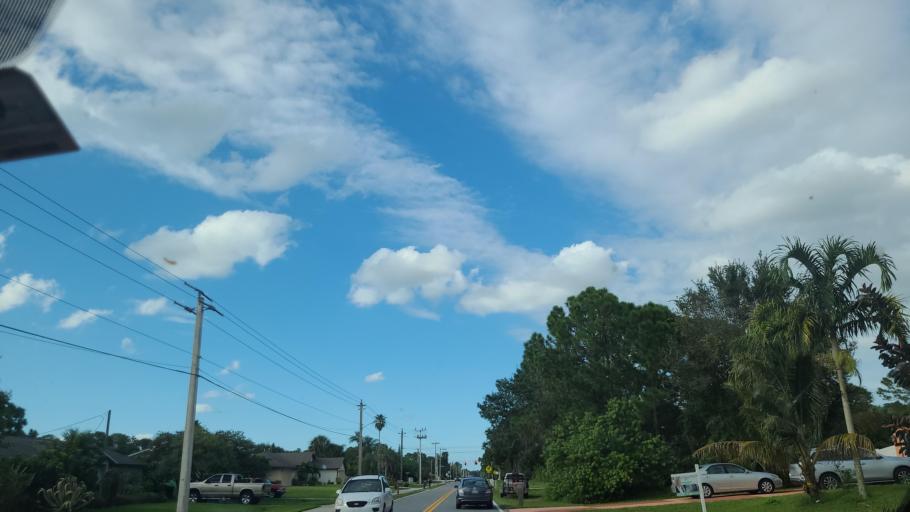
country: US
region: Florida
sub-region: Brevard County
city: West Melbourne
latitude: 27.9964
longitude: -80.6630
